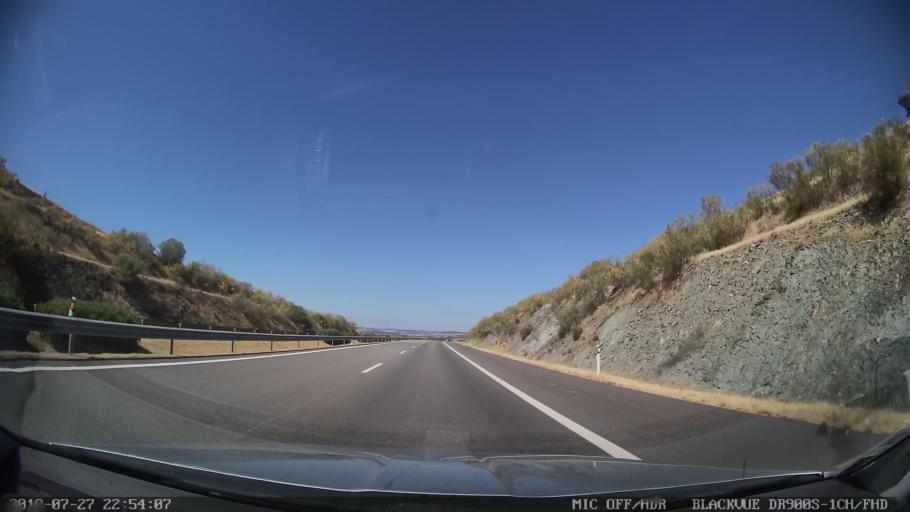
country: PT
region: Evora
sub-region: Vila Vicosa
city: Vila Vicosa
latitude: 38.8510
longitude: -7.3408
